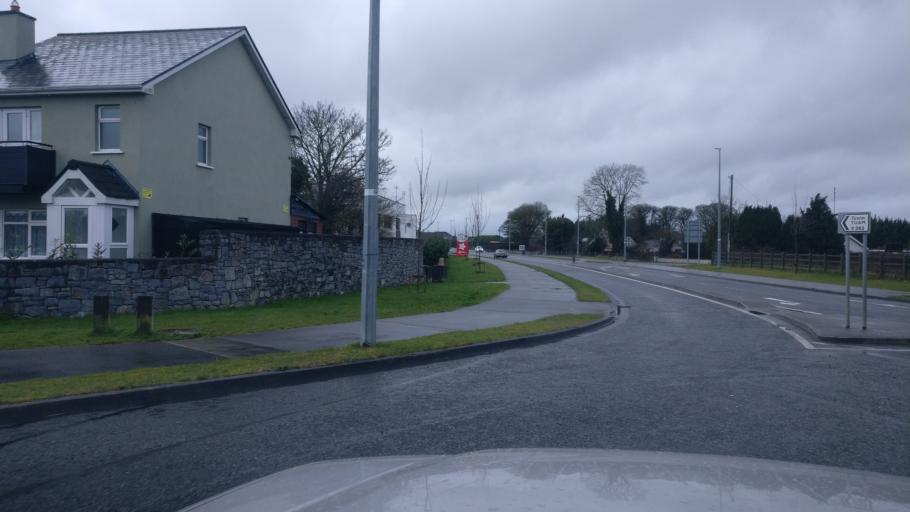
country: IE
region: Leinster
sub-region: An Iarmhi
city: Athlone
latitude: 53.4236
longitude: -7.9983
